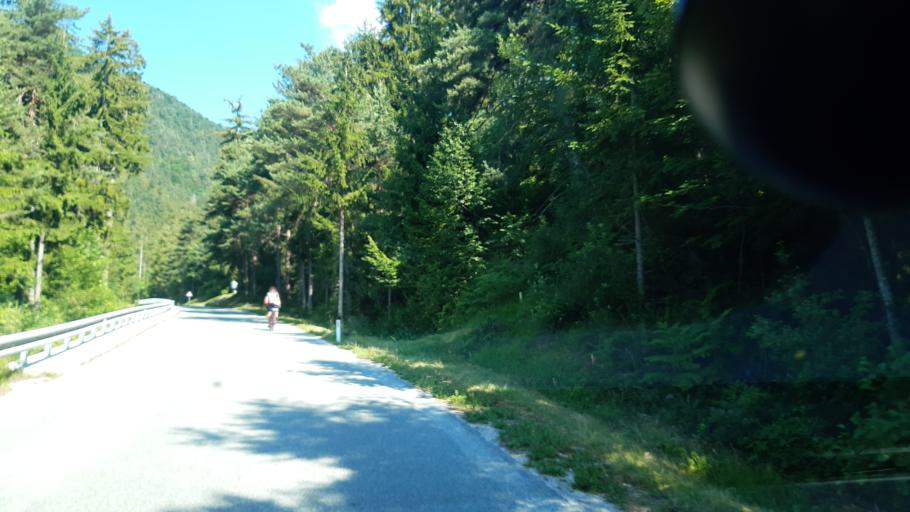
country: SI
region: Trzic
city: Bistrica pri Trzicu
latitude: 46.3614
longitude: 14.2862
